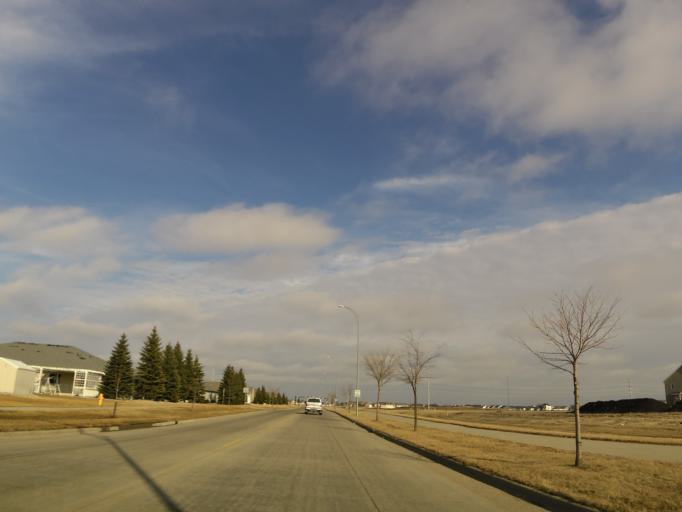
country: US
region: North Dakota
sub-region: Grand Forks County
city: Grand Forks
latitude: 47.8821
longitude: -97.0728
